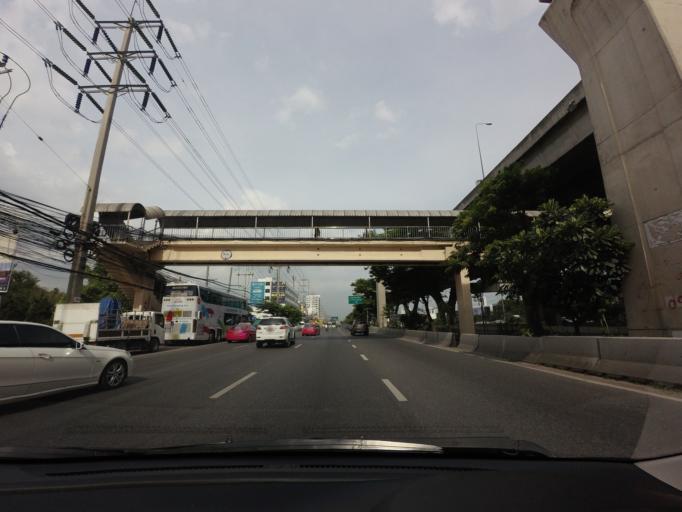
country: TH
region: Bangkok
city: Bang Na
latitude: 13.6648
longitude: 100.6515
